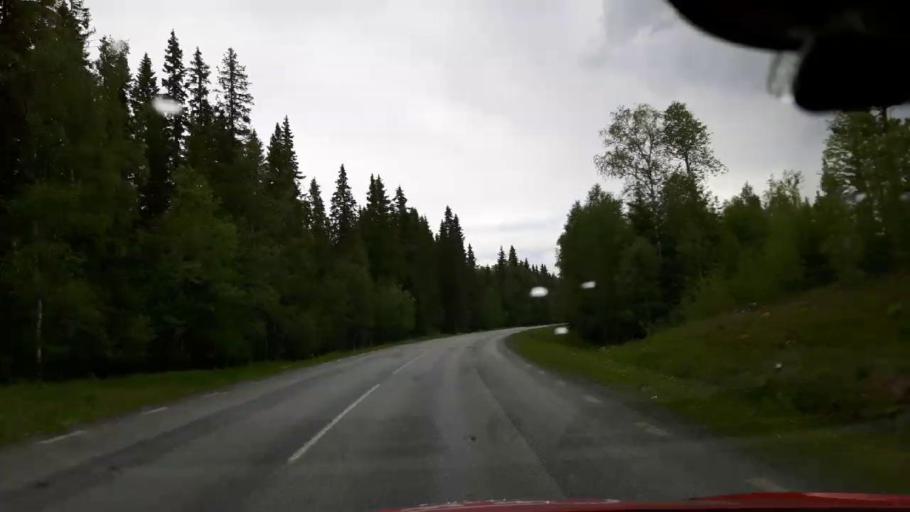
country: SE
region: Jaemtland
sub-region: Krokoms Kommun
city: Krokom
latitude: 63.4293
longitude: 14.2098
